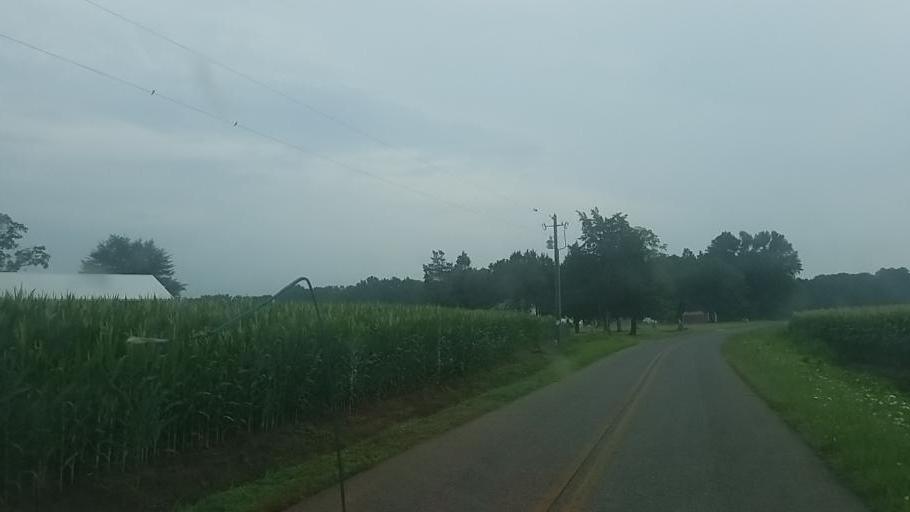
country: US
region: Delaware
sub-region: Sussex County
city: Selbyville
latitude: 38.4226
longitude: -75.3093
